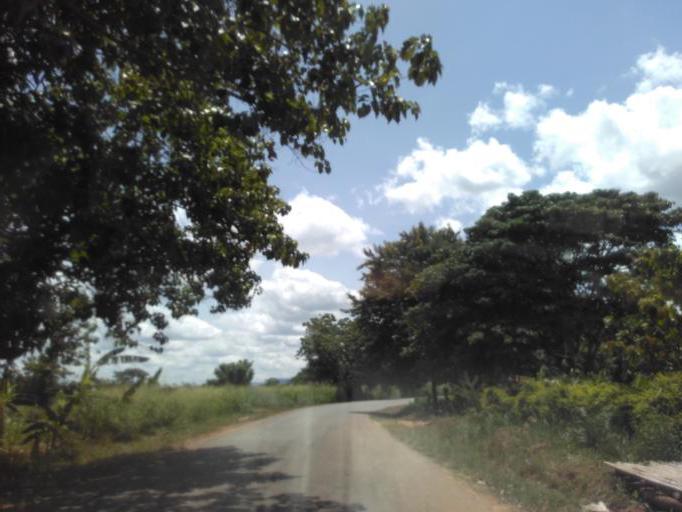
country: GH
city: Akropong
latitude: 6.0962
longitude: -0.1021
